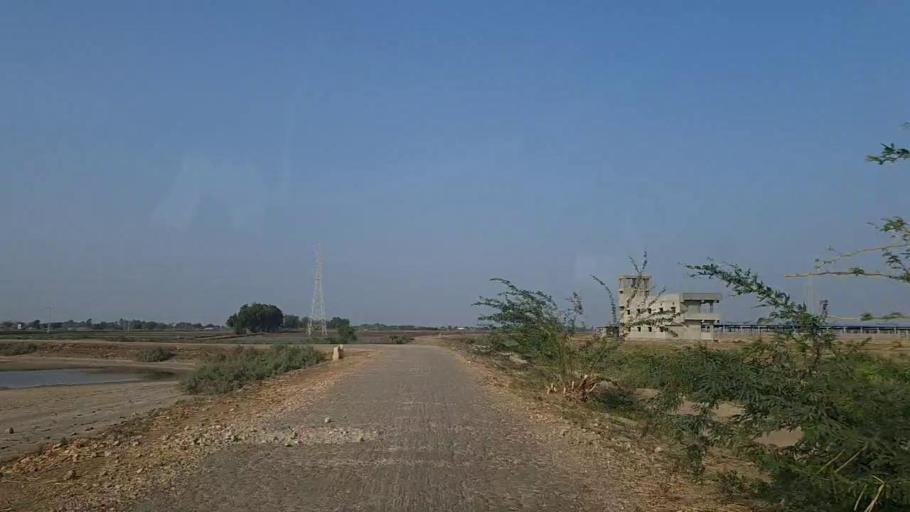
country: PK
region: Sindh
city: Mirpur Sakro
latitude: 24.5619
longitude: 67.6710
